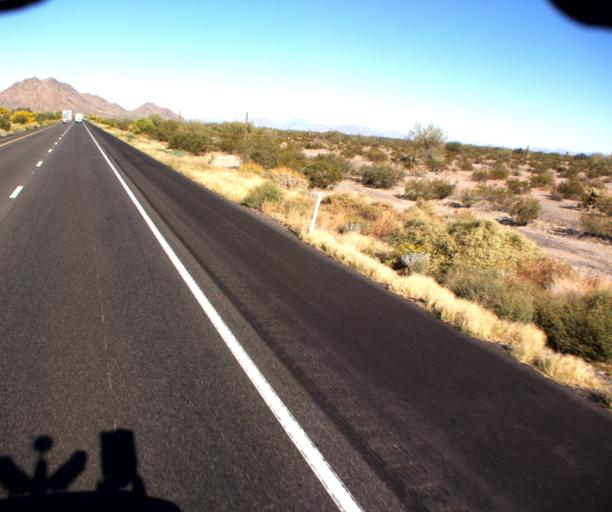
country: US
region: Arizona
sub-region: Maricopa County
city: Gila Bend
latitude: 32.9025
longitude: -112.5201
